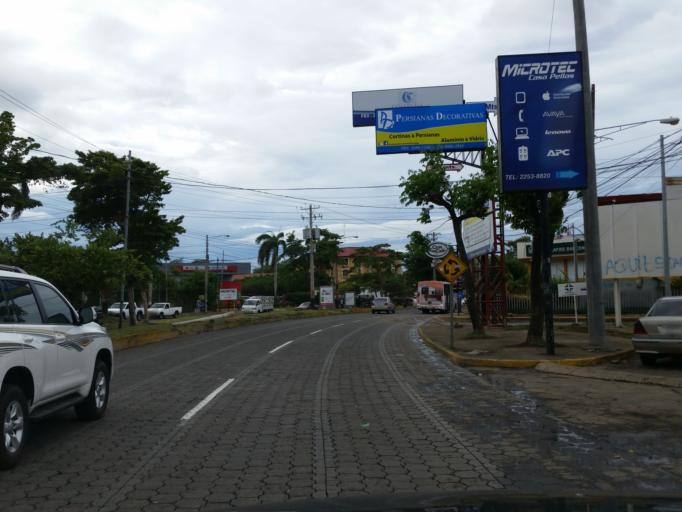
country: NI
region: Managua
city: Managua
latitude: 12.1324
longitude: -86.2809
